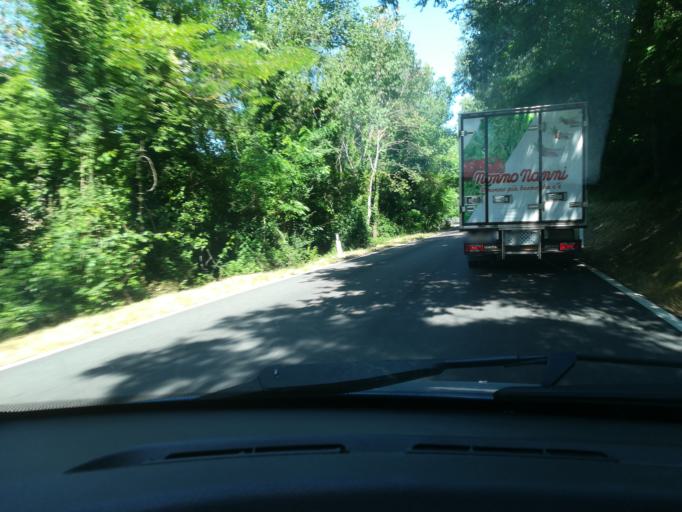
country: IT
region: The Marches
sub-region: Provincia di Macerata
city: Ripe San Ginesio
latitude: 43.1127
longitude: 13.3630
